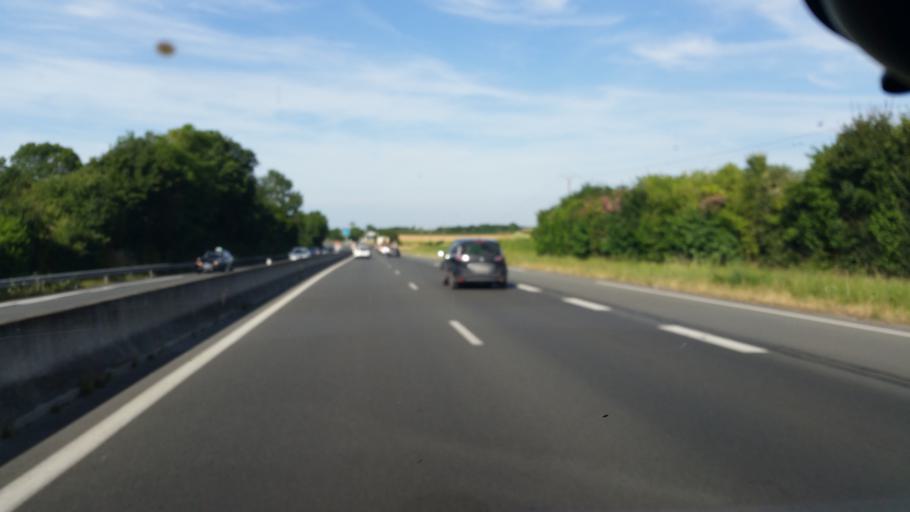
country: FR
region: Poitou-Charentes
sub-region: Departement de la Charente-Maritime
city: Dompierre-sur-Mer
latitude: 46.1821
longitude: -1.0864
